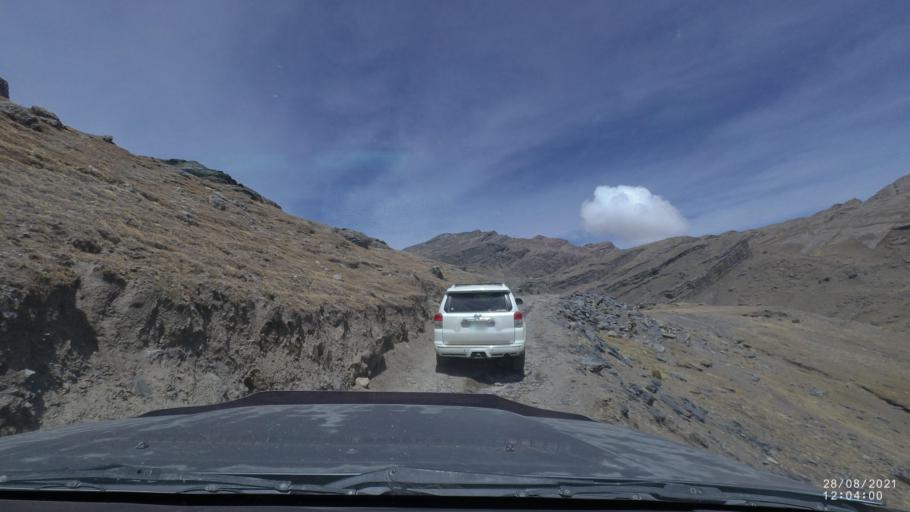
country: BO
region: Cochabamba
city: Sipe Sipe
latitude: -17.2658
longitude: -66.3843
